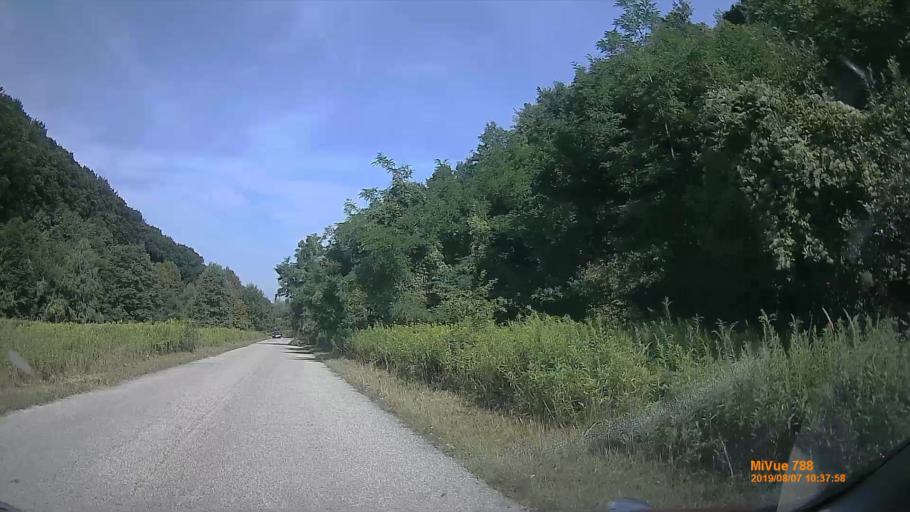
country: HU
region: Veszprem
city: Ajka
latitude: 47.0726
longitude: 17.5825
